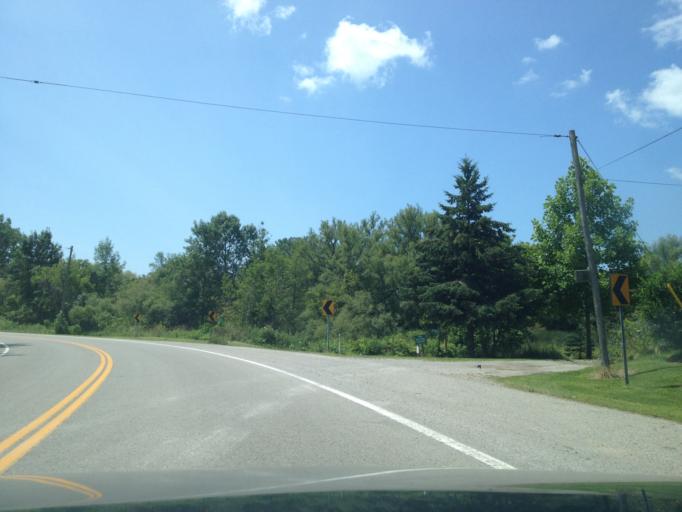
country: CA
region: Ontario
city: Norfolk County
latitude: 42.5979
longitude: -80.4844
